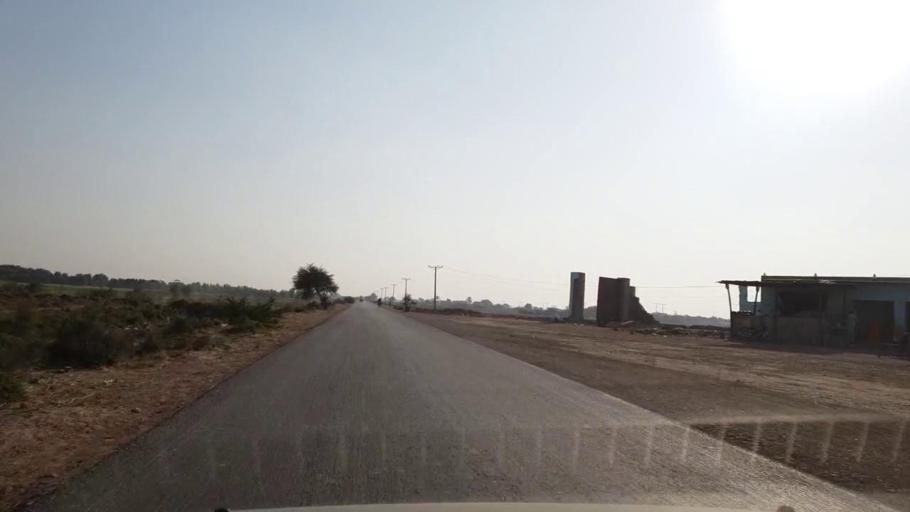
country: PK
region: Sindh
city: Bulri
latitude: 24.9045
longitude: 68.3469
